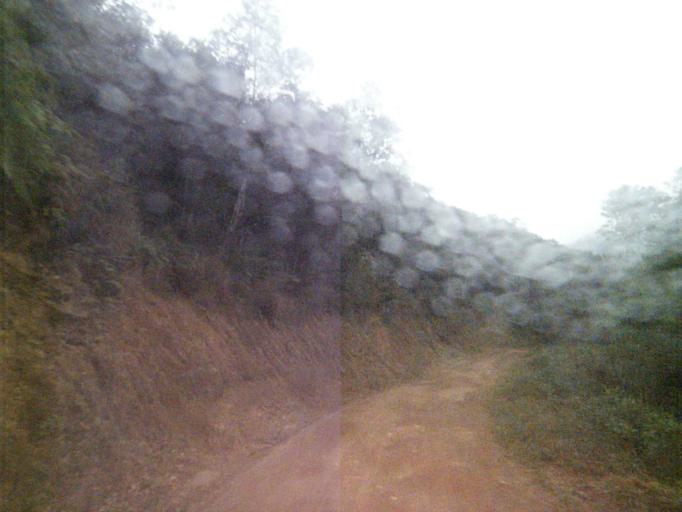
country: BR
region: Santa Catarina
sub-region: Anitapolis
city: Anitapolis
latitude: -27.8736
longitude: -49.1323
